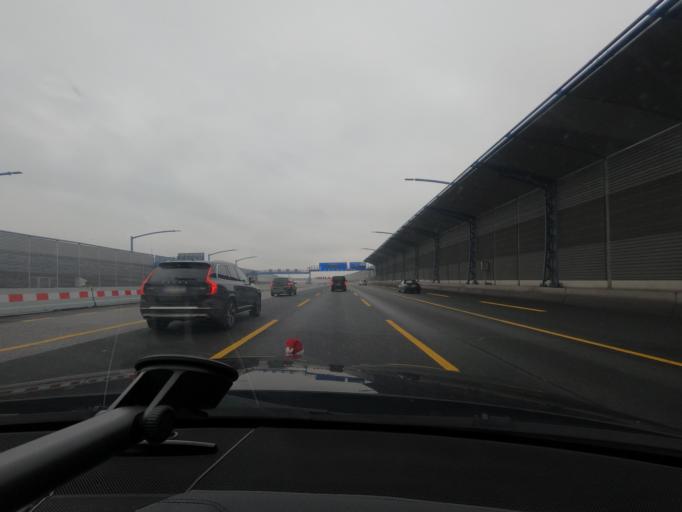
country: DE
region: Hamburg
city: Stellingen
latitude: 53.5931
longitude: 9.9196
